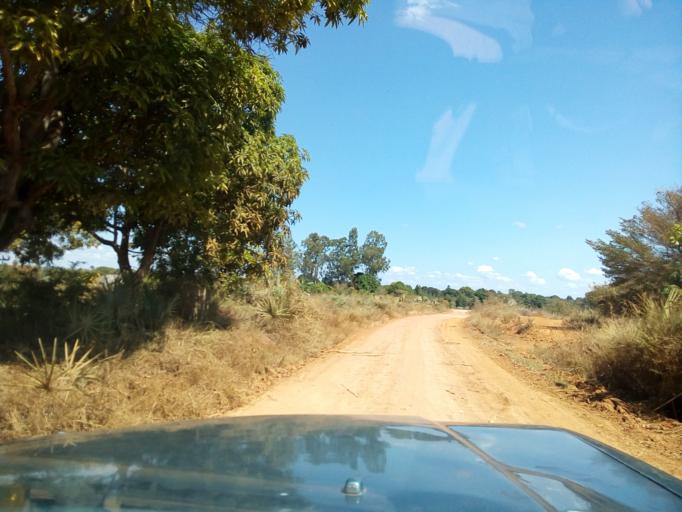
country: MG
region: Boeny
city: Mahajanga
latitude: -15.9604
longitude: 45.9670
